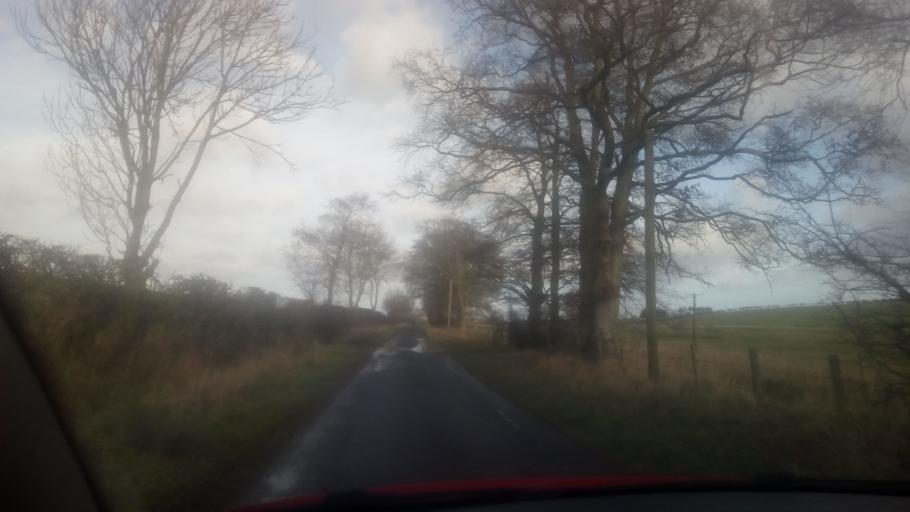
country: GB
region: Scotland
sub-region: The Scottish Borders
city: Kelso
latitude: 55.4980
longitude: -2.4270
